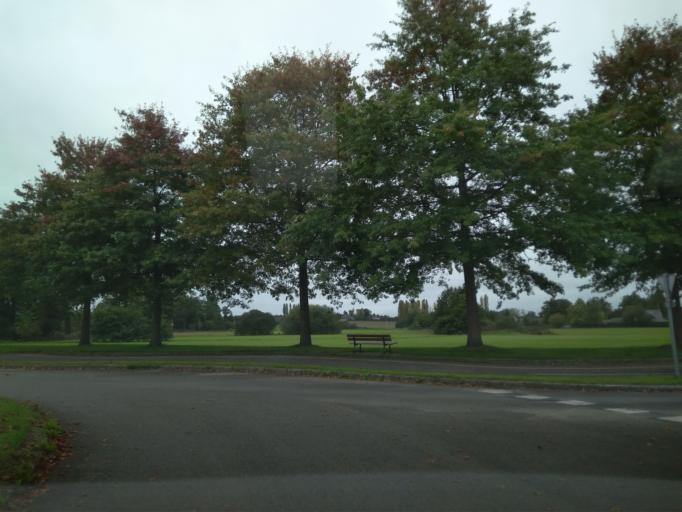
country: FR
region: Brittany
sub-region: Departement d'Ille-et-Vilaine
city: Betton
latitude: 48.1721
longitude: -1.6375
